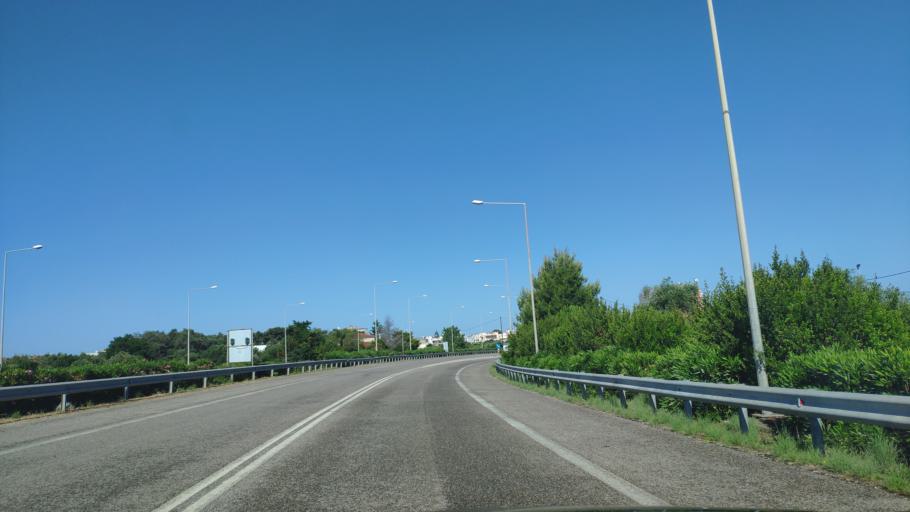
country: GR
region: Epirus
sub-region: Nomos Prevezis
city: Preveza
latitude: 38.9486
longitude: 20.7416
